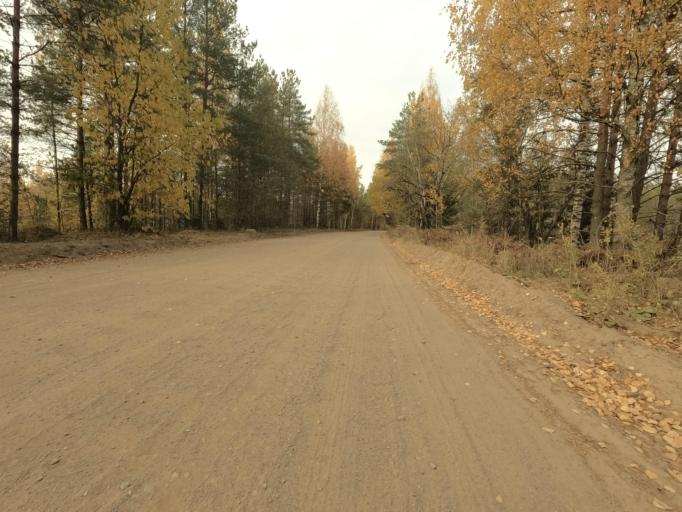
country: RU
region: Leningrad
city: Priladozhskiy
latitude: 59.6807
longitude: 31.3638
